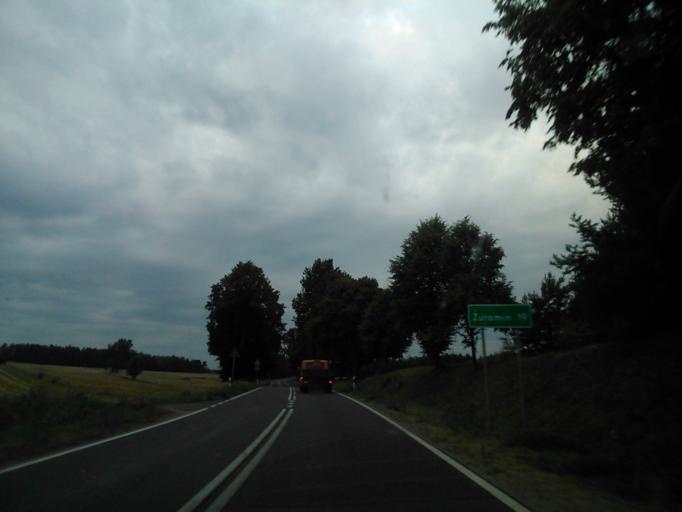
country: PL
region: Masovian Voivodeship
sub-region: Powiat mlawski
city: Lipowiec Koscielny
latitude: 53.1023
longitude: 20.1675
